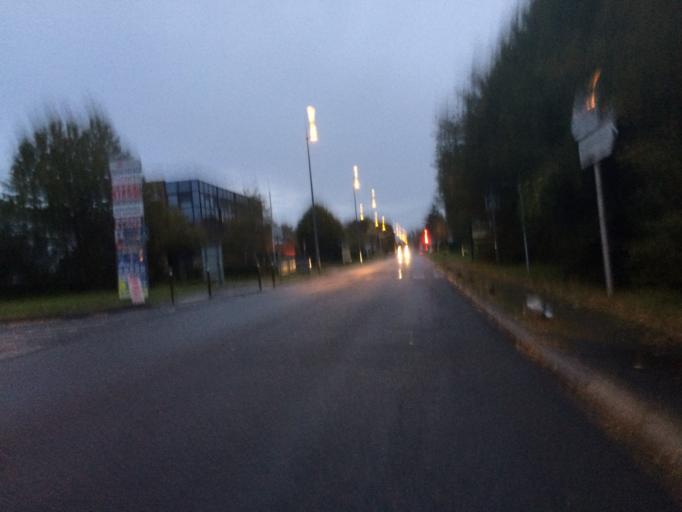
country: FR
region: Ile-de-France
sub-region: Departement de l'Essonne
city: Orsay
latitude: 48.6885
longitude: 2.2040
